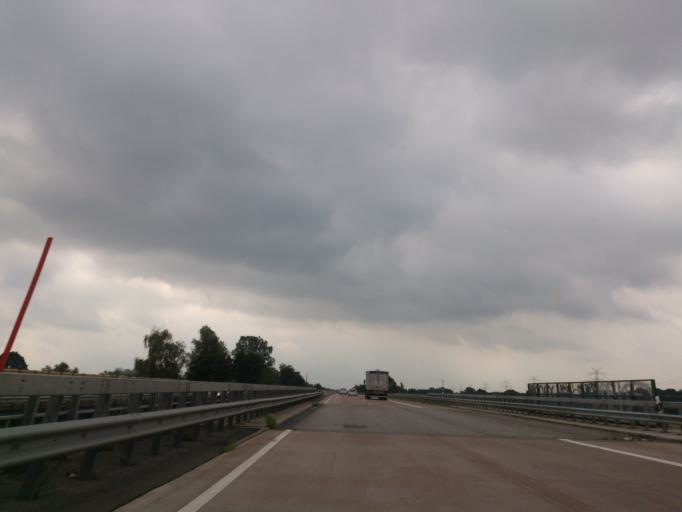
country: DE
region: Schleswig-Holstein
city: Horst
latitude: 53.8226
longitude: 9.6451
